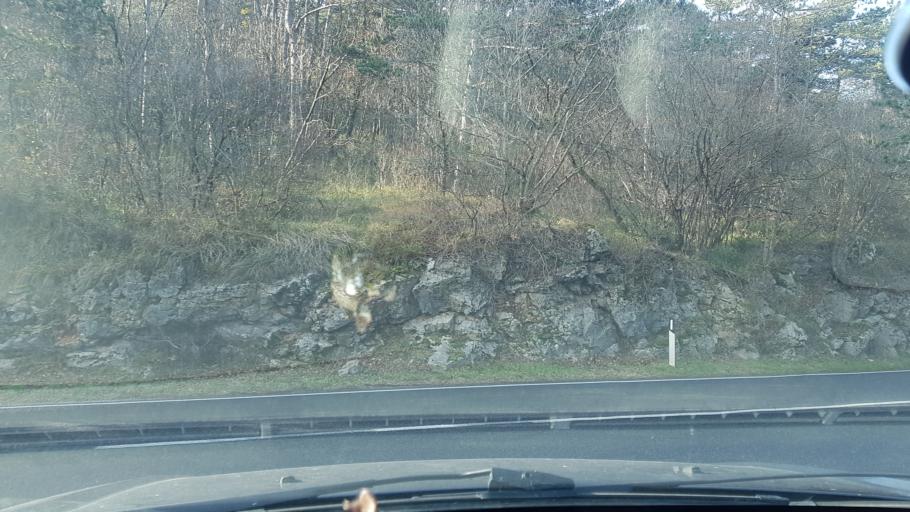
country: IT
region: Friuli Venezia Giulia
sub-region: Provincia di Gorizia
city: Doberdo del Lago
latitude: 45.8373
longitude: 13.5658
